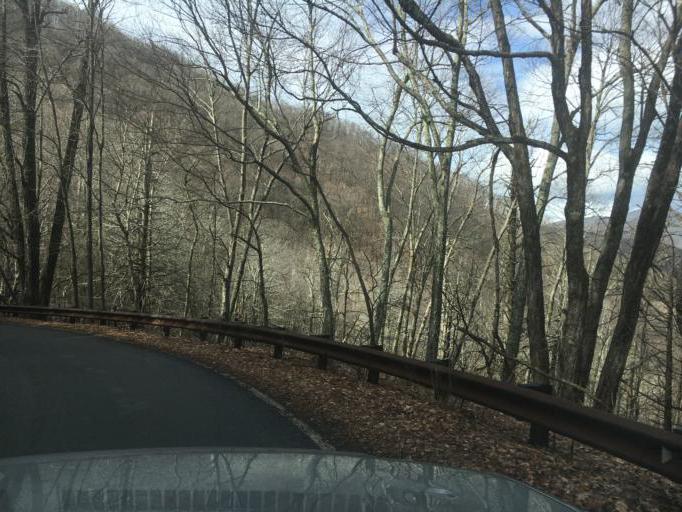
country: US
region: North Carolina
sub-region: Transylvania County
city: Brevard
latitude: 35.3675
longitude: -82.8012
